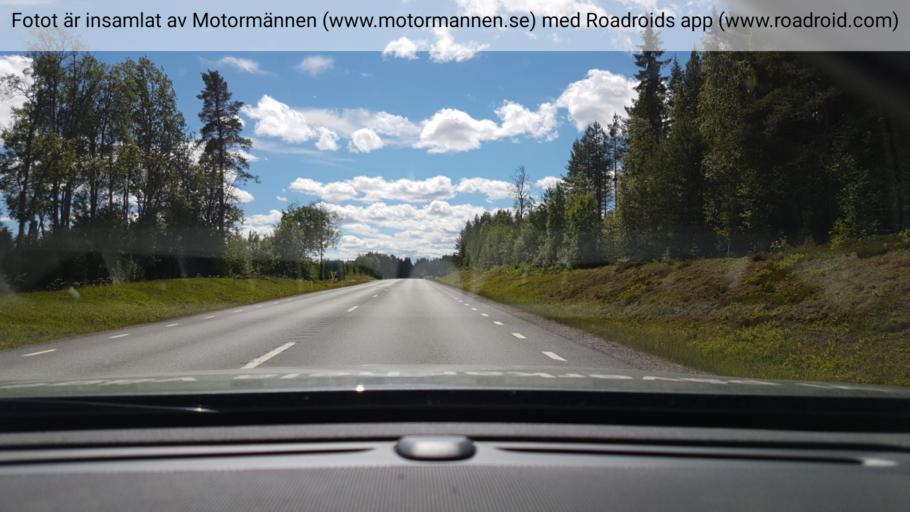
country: SE
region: Vaesterbotten
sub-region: Skelleftea Kommun
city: Burea
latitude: 64.3553
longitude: 21.2946
